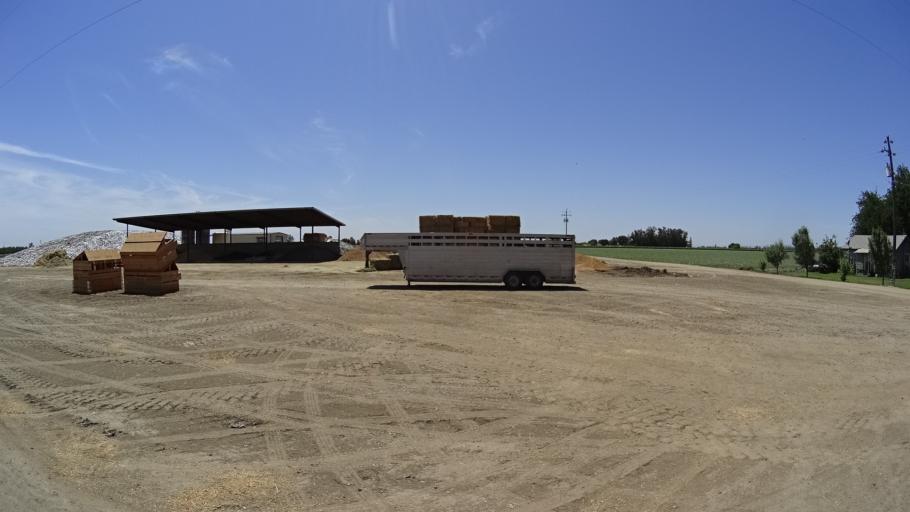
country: US
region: California
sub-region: Kings County
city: Lemoore
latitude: 36.3498
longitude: -119.7851
